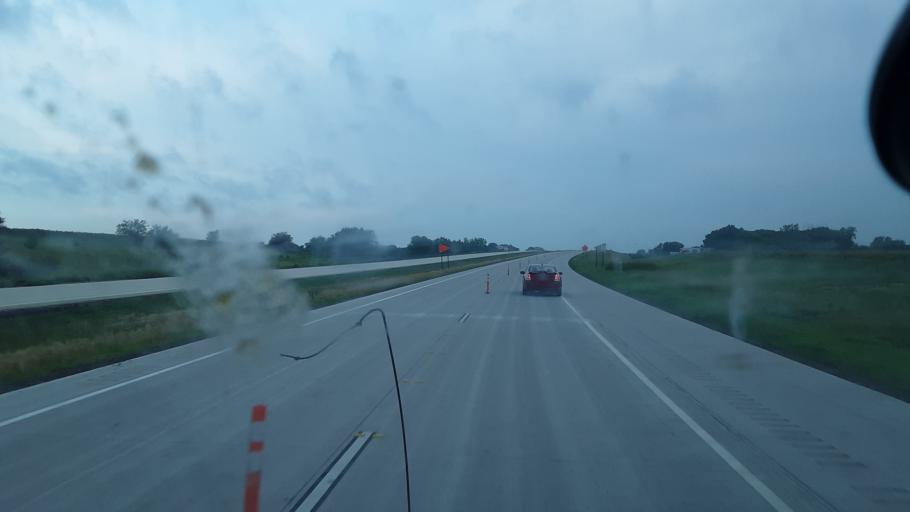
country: US
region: Minnesota
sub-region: Martin County
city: Fairmont
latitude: 43.6708
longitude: -94.4106
